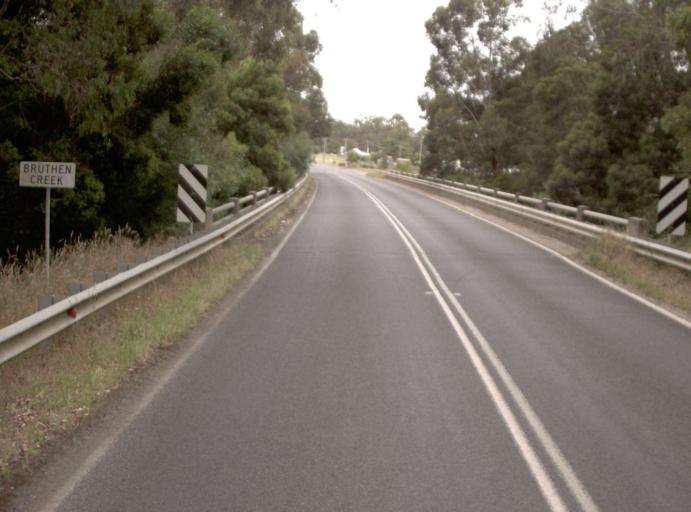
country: AU
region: Victoria
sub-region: Wellington
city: Sale
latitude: -38.5254
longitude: 146.8721
